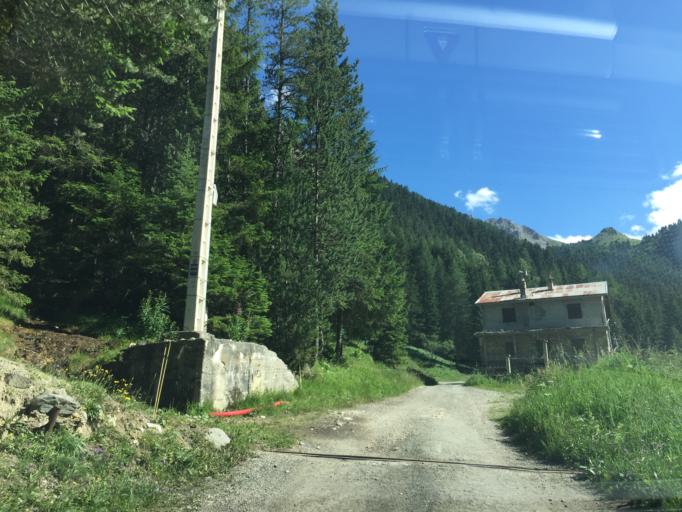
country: FR
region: Rhone-Alpes
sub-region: Departement de la Savoie
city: Modane
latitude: 45.1629
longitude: 6.6473
